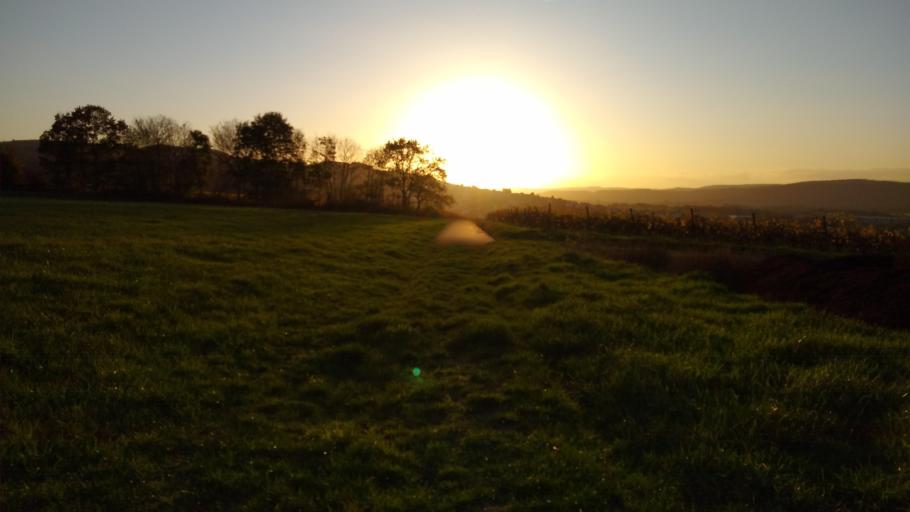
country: DE
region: Rheinland-Pfalz
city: Bekond
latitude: 49.8536
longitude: 6.8194
